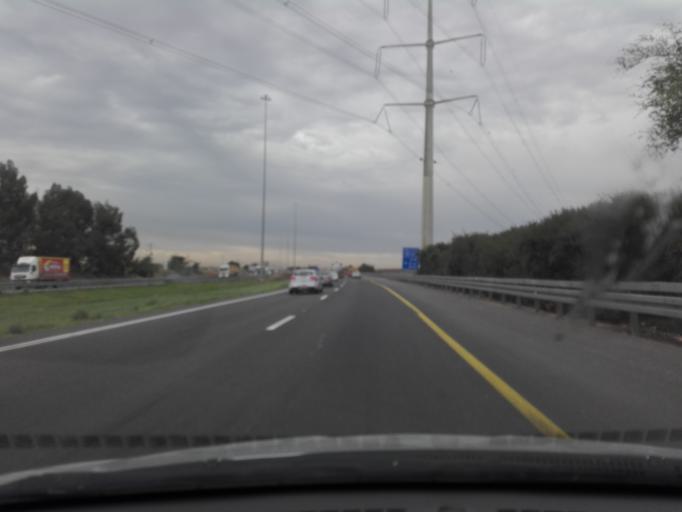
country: IL
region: Central District
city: Ramla
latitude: 31.8994
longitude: 34.8840
